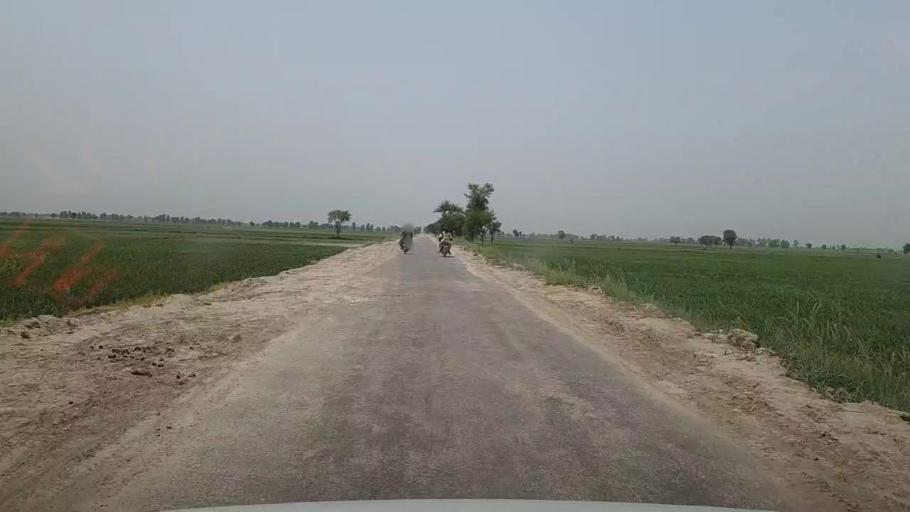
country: PK
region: Sindh
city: Sita Road
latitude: 27.0822
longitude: 67.9107
